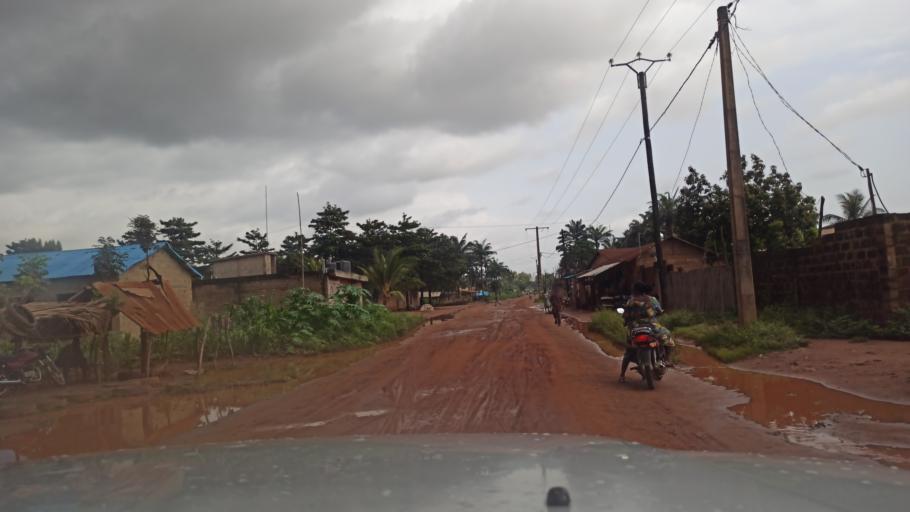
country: BJ
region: Queme
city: Porto-Novo
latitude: 6.5589
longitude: 2.5915
